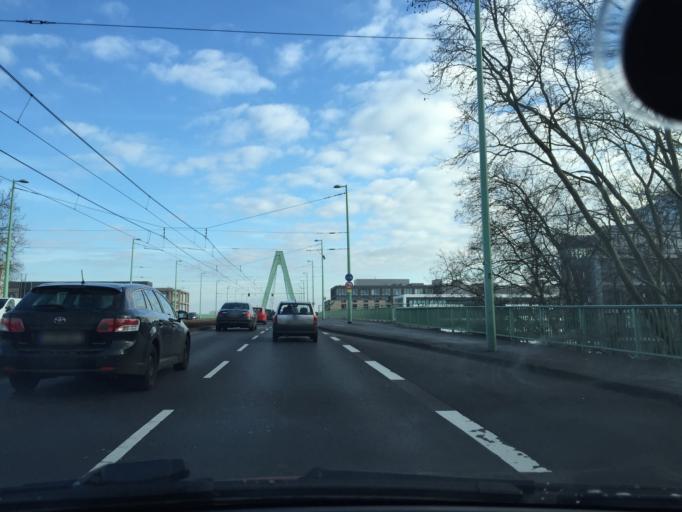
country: DE
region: North Rhine-Westphalia
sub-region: Regierungsbezirk Koln
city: Altstadt Sud
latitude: 50.9300
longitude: 6.9620
